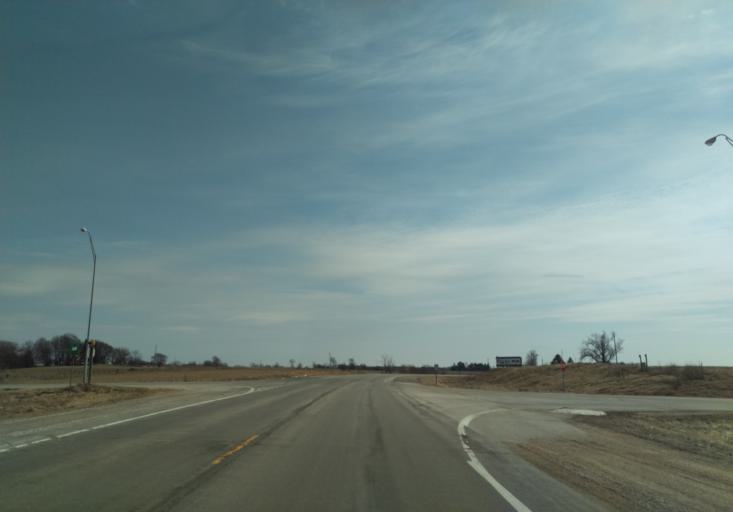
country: US
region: Iowa
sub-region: Winneshiek County
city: Decorah
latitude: 43.3681
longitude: -91.8070
